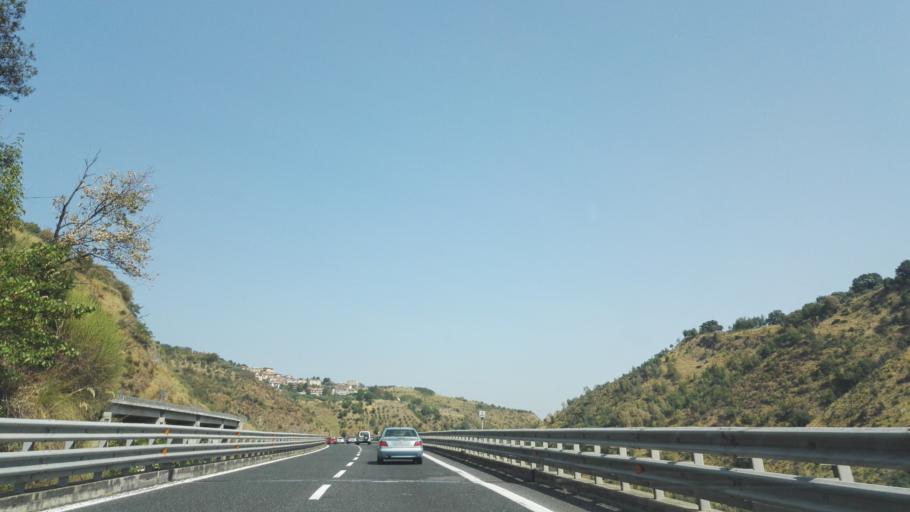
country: IT
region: Calabria
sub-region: Provincia di Cosenza
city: Laurignano
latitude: 39.2642
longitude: 16.2507
